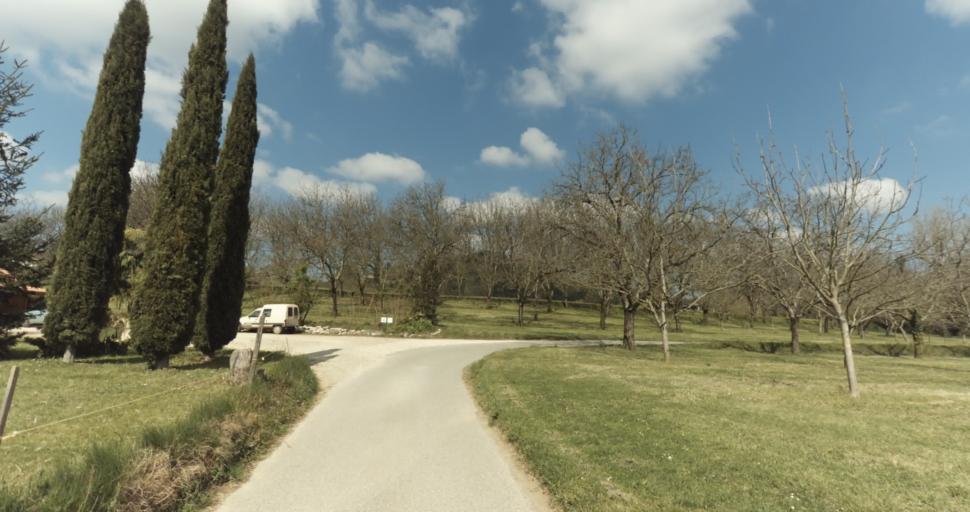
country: FR
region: Rhone-Alpes
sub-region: Departement de l'Isere
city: Saint-Verand
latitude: 45.1627
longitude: 5.3291
